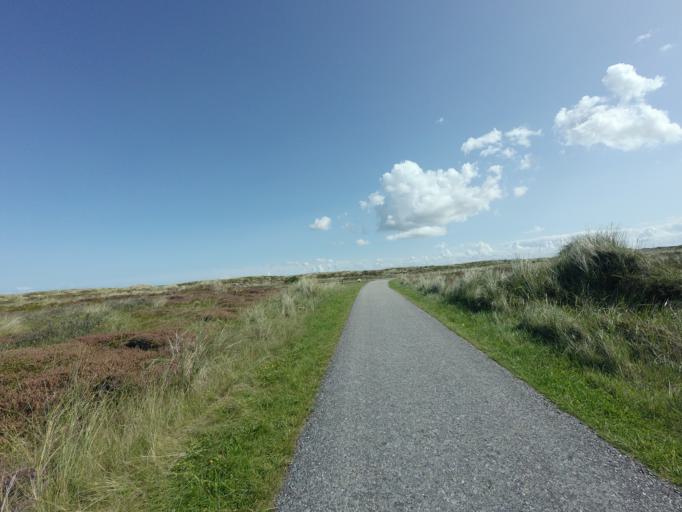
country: NL
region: Friesland
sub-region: Gemeente Terschelling
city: West-Terschelling
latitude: 53.4167
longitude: 5.3871
